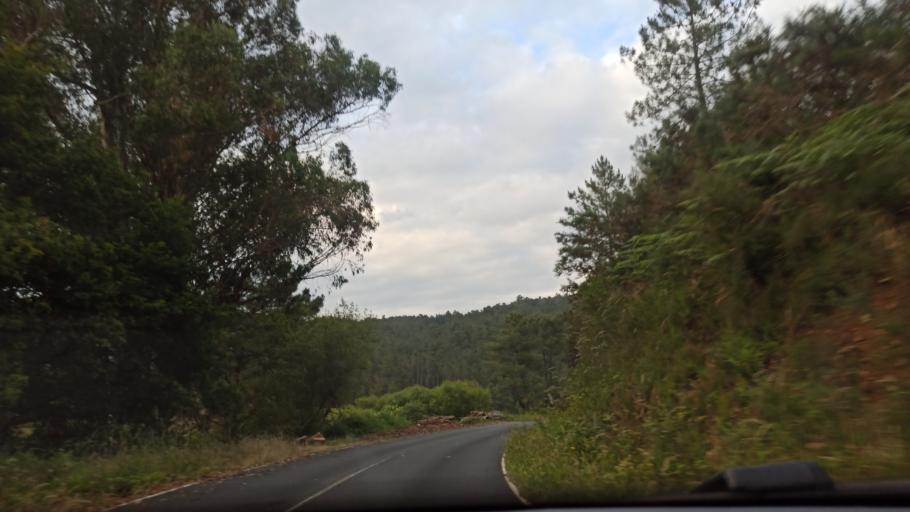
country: ES
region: Galicia
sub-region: Provincia da Coruna
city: Santiso
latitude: 42.8187
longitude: -8.1275
